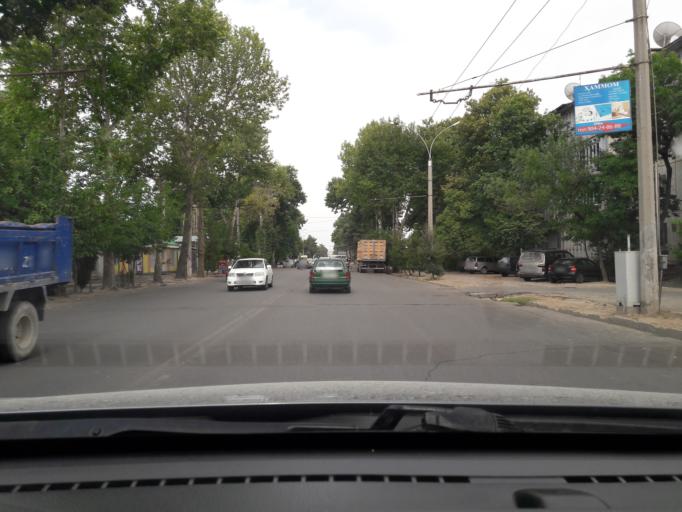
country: TJ
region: Dushanbe
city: Dushanbe
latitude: 38.5461
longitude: 68.7515
